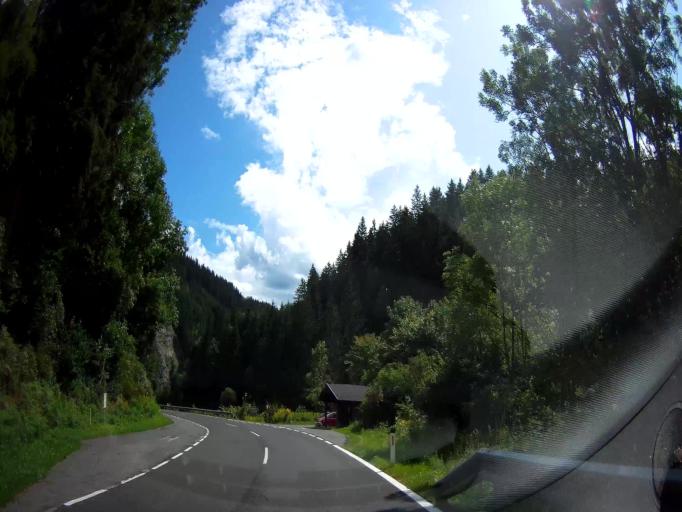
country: AT
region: Carinthia
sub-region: Politischer Bezirk Spittal an der Drau
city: Seeboden
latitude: 46.8508
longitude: 13.5006
